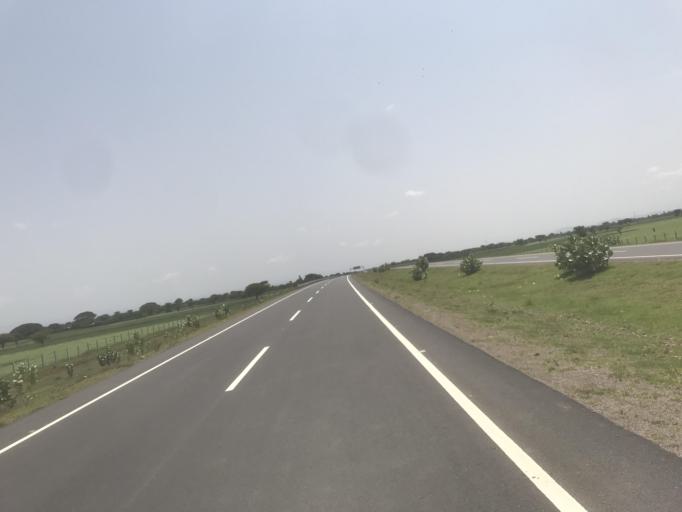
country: ET
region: Oromiya
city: Mojo
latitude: 8.2883
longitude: 38.9209
